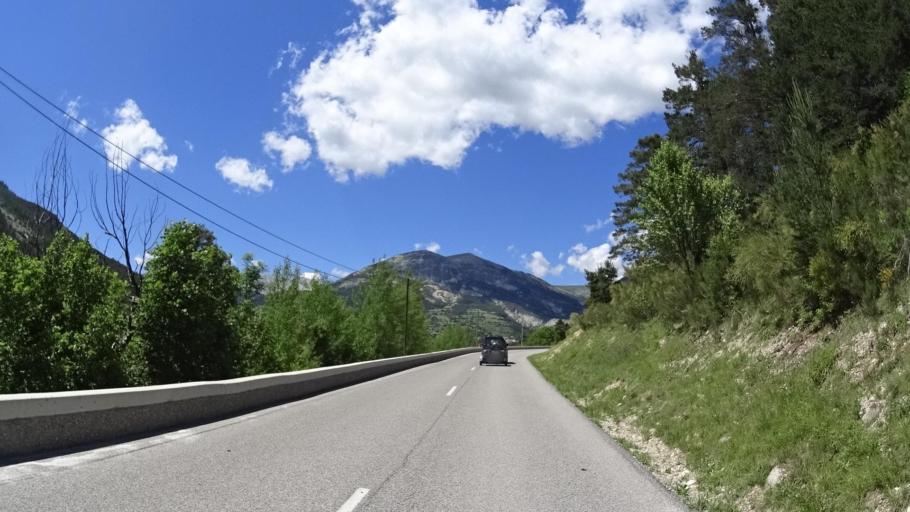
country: FR
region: Provence-Alpes-Cote d'Azur
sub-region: Departement des Alpes-de-Haute-Provence
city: Annot
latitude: 44.0778
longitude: 6.5690
